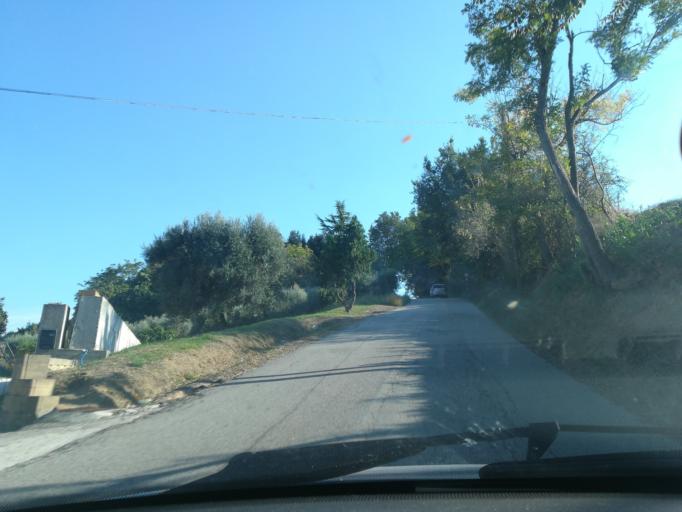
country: IT
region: The Marches
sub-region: Provincia di Macerata
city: Macerata
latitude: 43.3043
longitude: 13.4783
